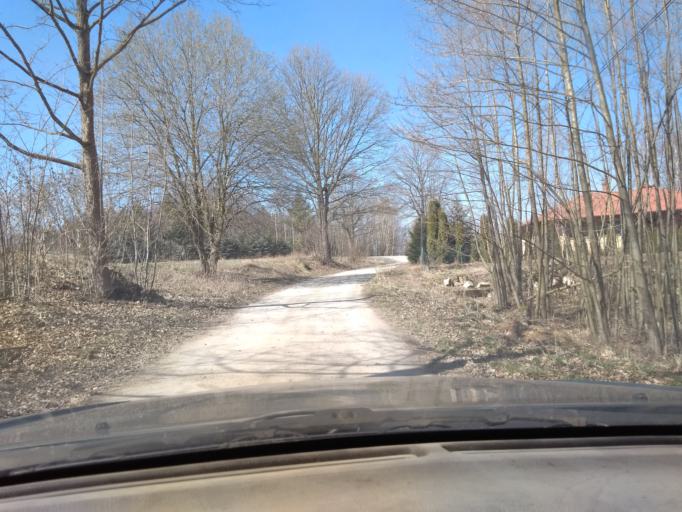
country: PL
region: Lower Silesian Voivodeship
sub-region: Powiat jeleniogorski
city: Sosnowka
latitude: 50.8378
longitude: 15.7404
